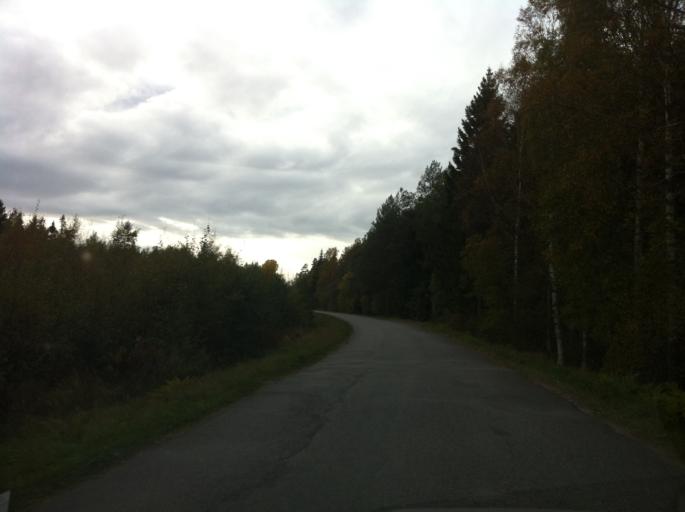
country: SE
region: OEstergoetland
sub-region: Motala Kommun
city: Motala
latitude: 58.6175
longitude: 14.9574
